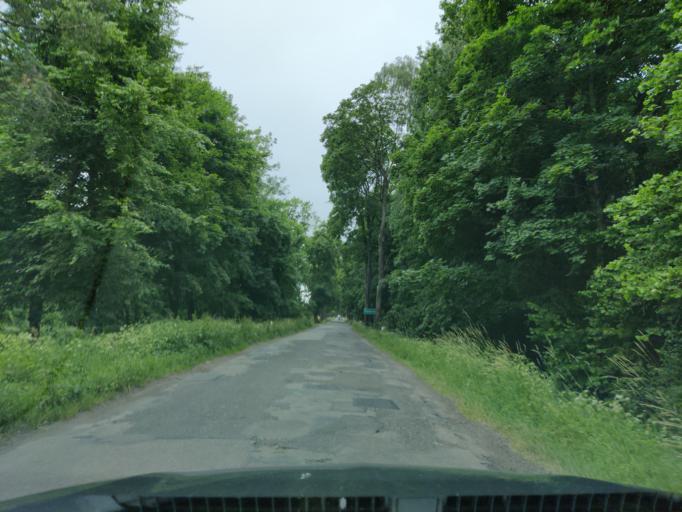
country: PL
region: Warmian-Masurian Voivodeship
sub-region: Powiat gizycki
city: Ryn
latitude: 53.9175
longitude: 21.5558
